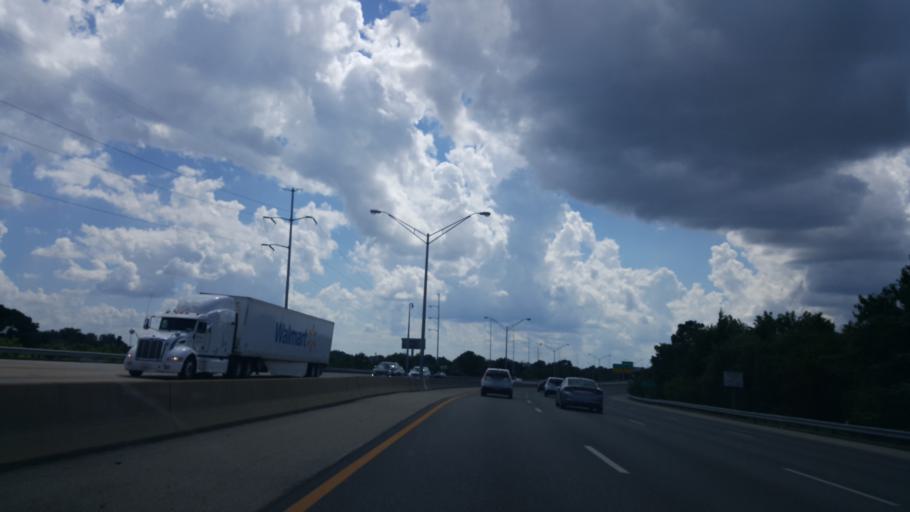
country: US
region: Virginia
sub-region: City of Newport News
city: Newport News
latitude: 36.9996
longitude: -76.4072
